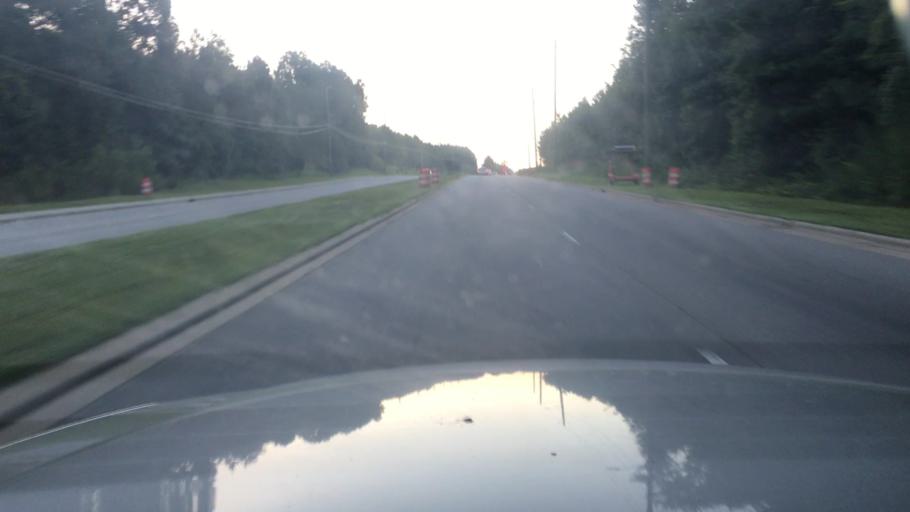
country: US
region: North Carolina
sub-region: Cumberland County
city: Fort Bragg
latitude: 35.0649
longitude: -79.0319
